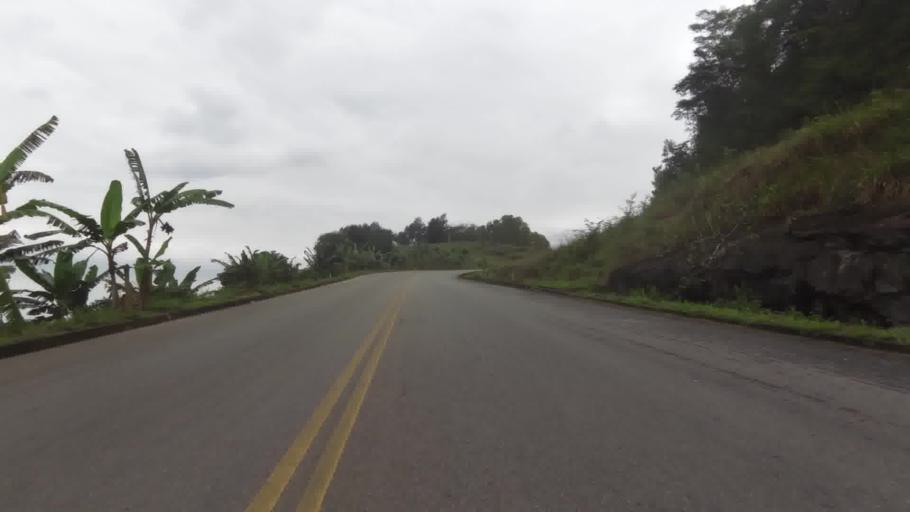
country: BR
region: Espirito Santo
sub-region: Iconha
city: Iconha
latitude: -20.7836
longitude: -40.8133
